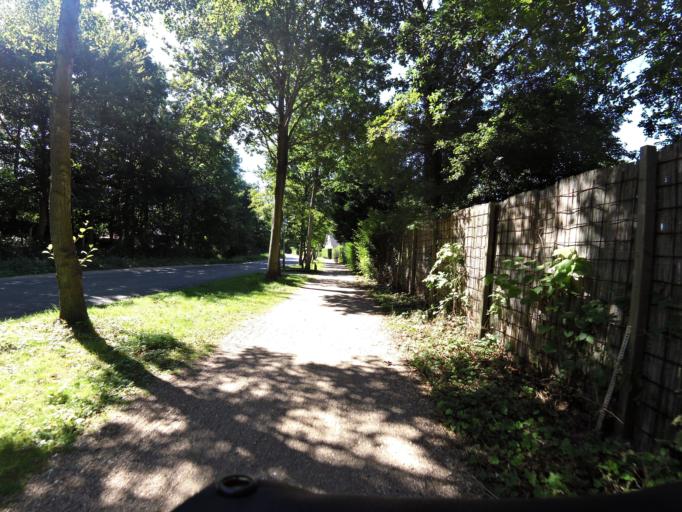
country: NL
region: Zeeland
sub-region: Schouwen-Duiveland
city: Renesse
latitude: 51.7269
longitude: 3.7551
